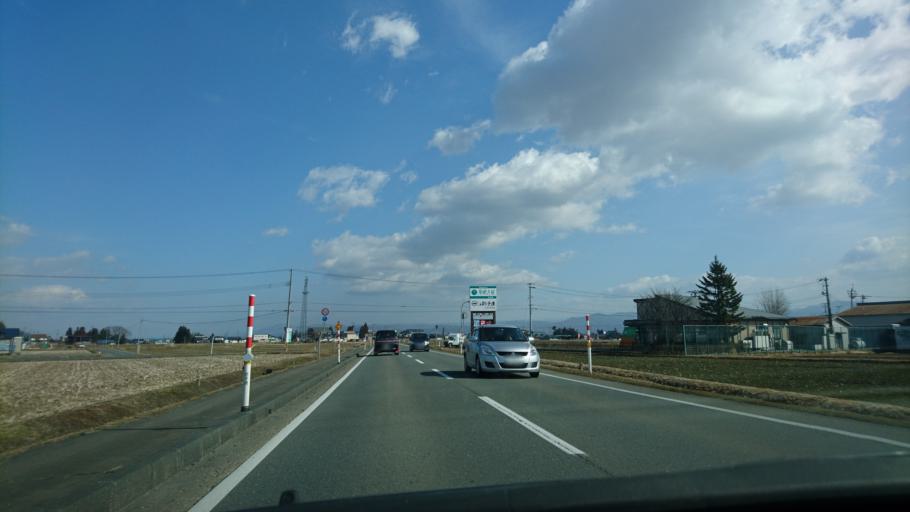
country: JP
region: Iwate
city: Morioka-shi
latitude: 39.5587
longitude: 141.1063
